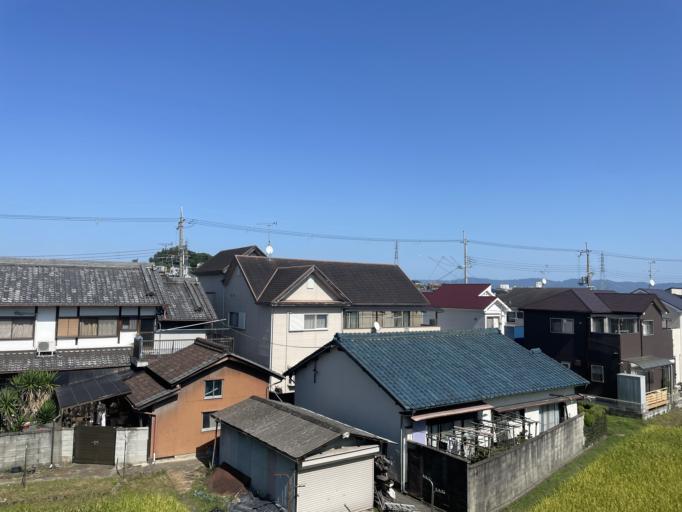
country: JP
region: Nara
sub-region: Ikoma-shi
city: Ikoma
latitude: 34.5960
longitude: 135.7097
